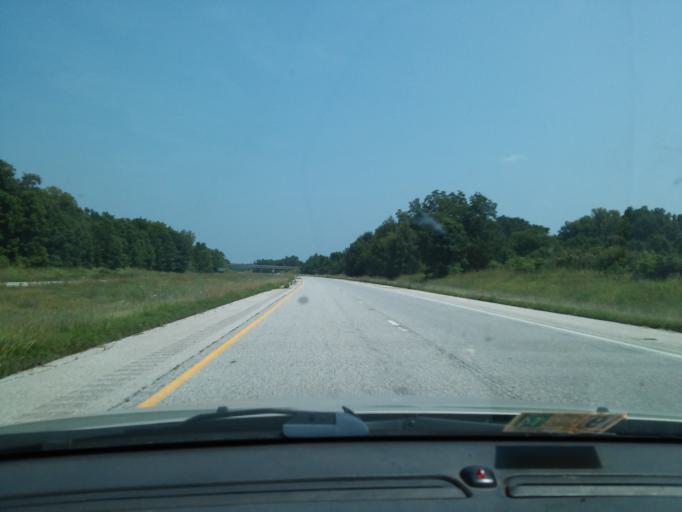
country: US
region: Illinois
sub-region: Pike County
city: Griggsville
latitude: 39.6741
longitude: -90.7487
